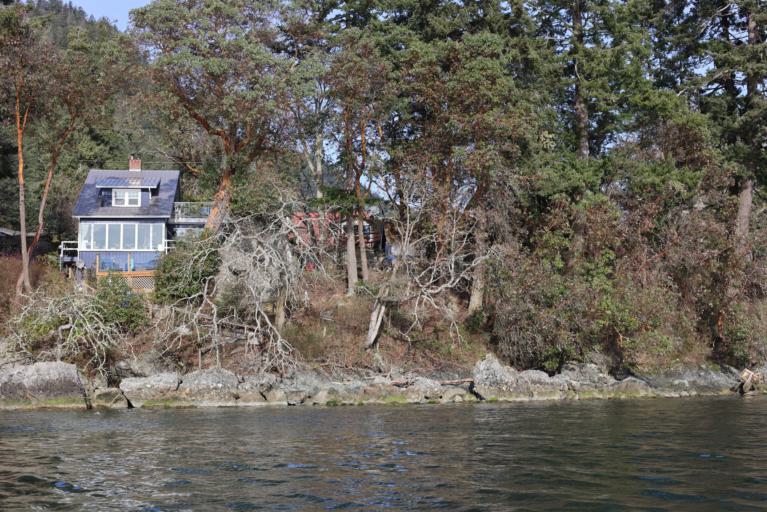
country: CA
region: British Columbia
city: Duncan
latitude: 48.7566
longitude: -123.5982
